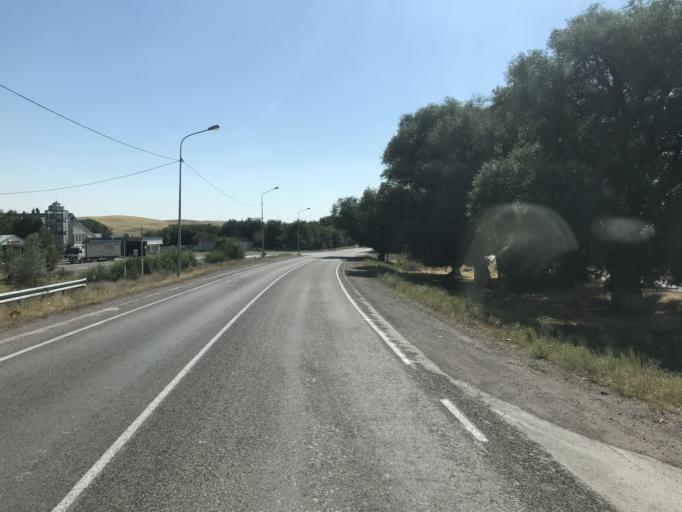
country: KZ
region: Zhambyl
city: Georgiyevka
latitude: 43.2412
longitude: 74.7769
